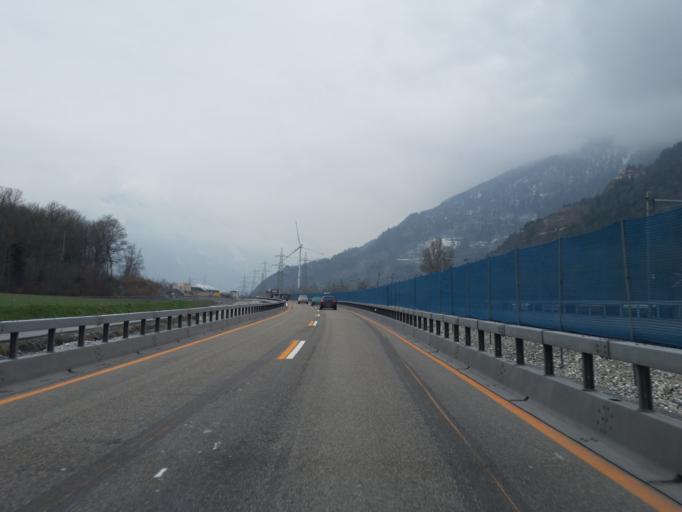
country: CH
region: Grisons
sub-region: Landquart District
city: Trimmis
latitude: 46.9059
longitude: 9.5496
